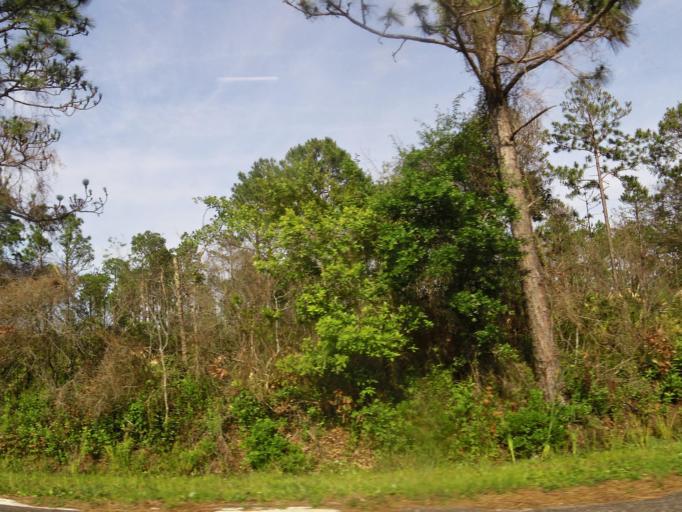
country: US
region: Florida
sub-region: Duval County
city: Atlantic Beach
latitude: 30.4727
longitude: -81.4865
